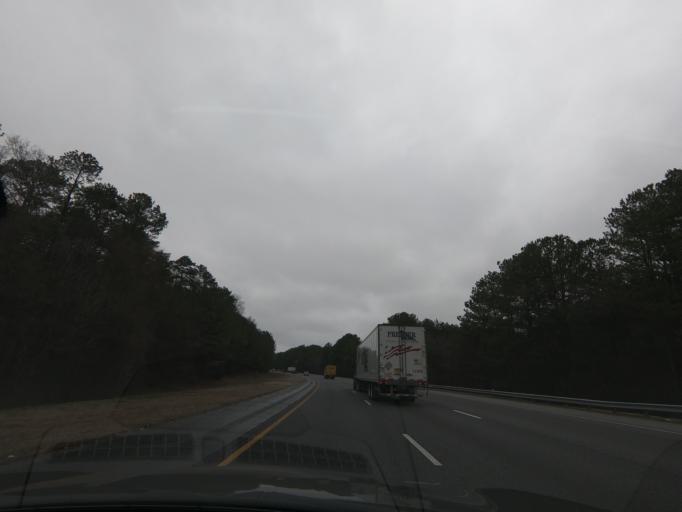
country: US
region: Georgia
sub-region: Bartow County
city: Adairsville
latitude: 34.4151
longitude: -84.9178
